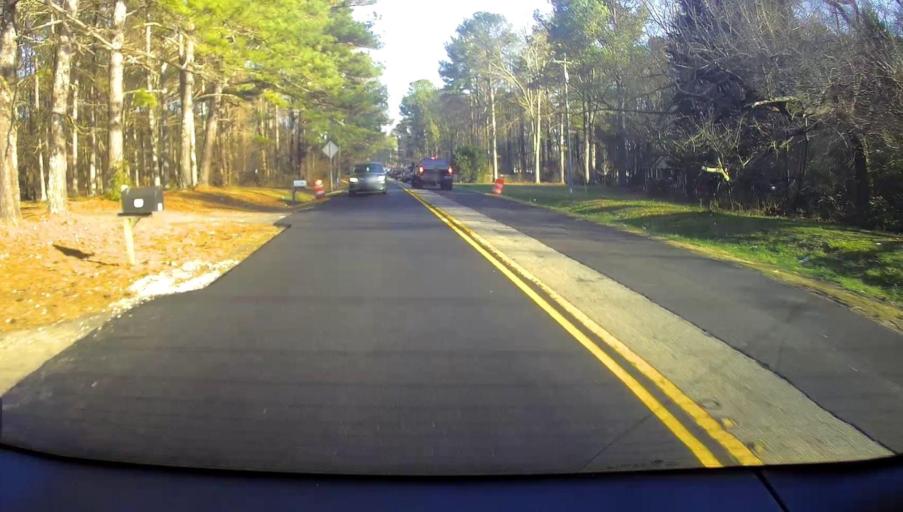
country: US
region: Georgia
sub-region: Clayton County
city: Irondale
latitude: 33.4541
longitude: -84.3730
